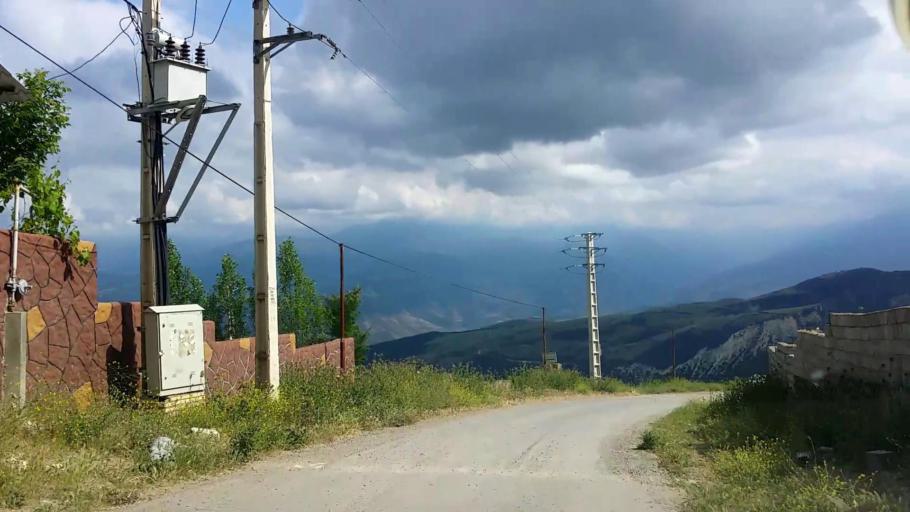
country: IR
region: Mazandaran
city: Chalus
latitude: 36.5543
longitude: 51.2893
